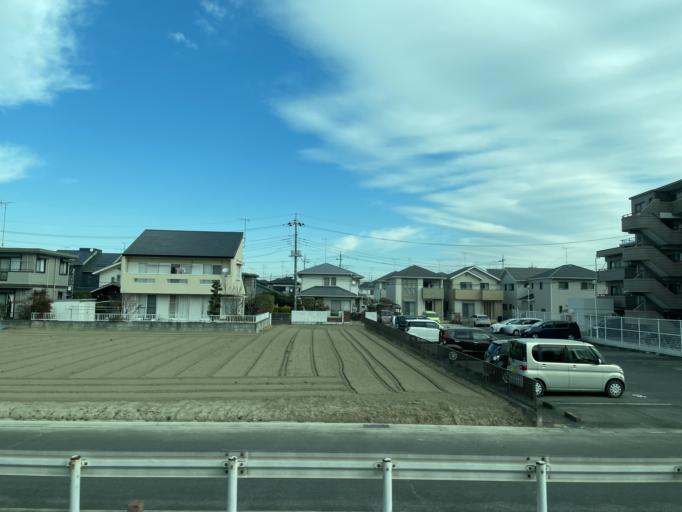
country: JP
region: Saitama
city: Fukiage-fujimi
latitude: 36.1173
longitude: 139.4287
